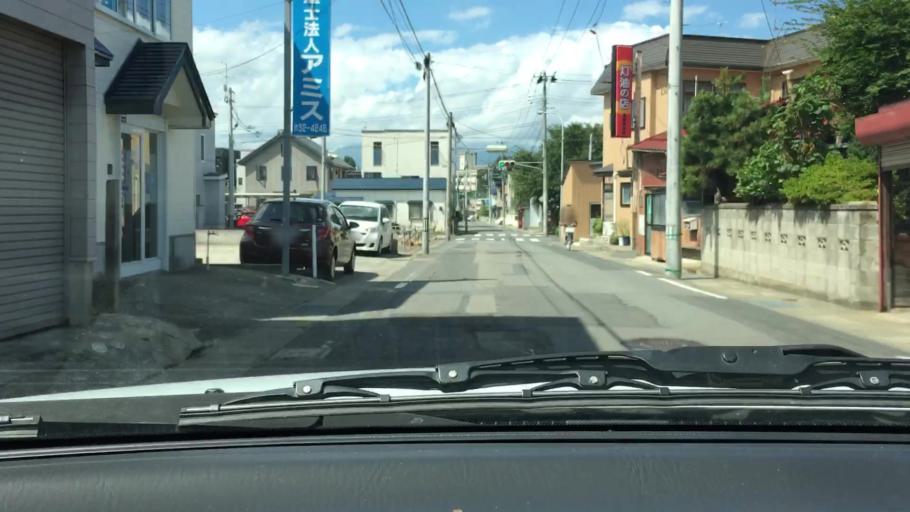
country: JP
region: Aomori
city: Hirosaki
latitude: 40.5934
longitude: 140.4727
